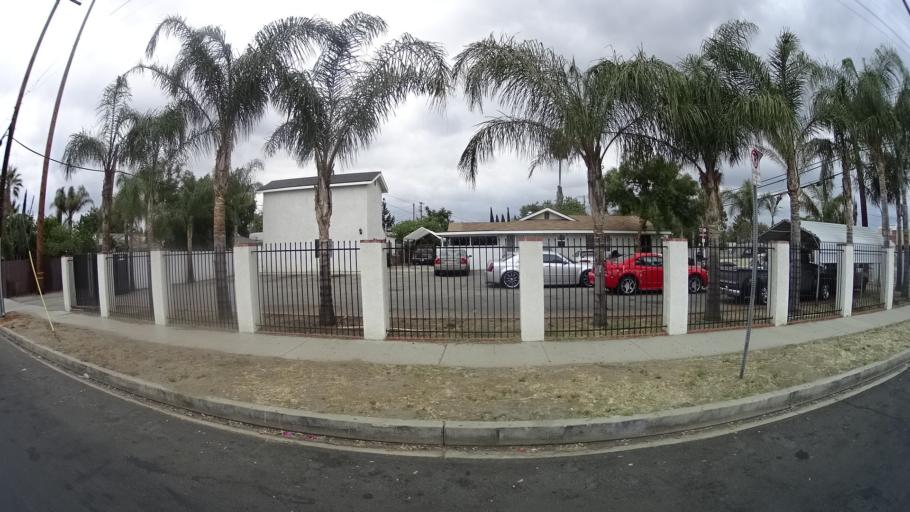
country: US
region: California
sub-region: Los Angeles County
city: San Fernando
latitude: 34.2518
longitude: -118.4422
